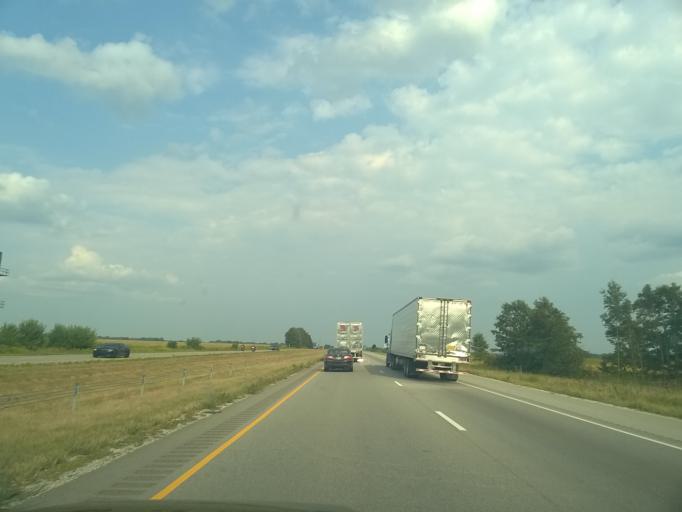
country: US
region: Indiana
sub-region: Clay County
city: Brazil
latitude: 39.4502
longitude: -87.1591
